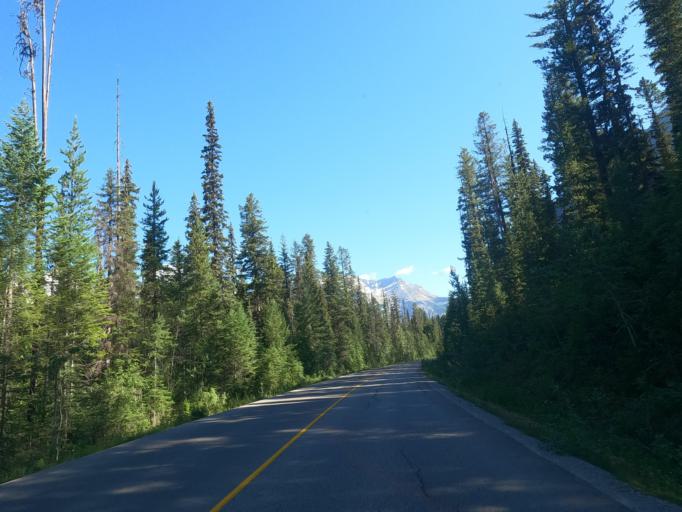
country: CA
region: Alberta
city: Lake Louise
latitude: 51.4072
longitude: -116.5361
